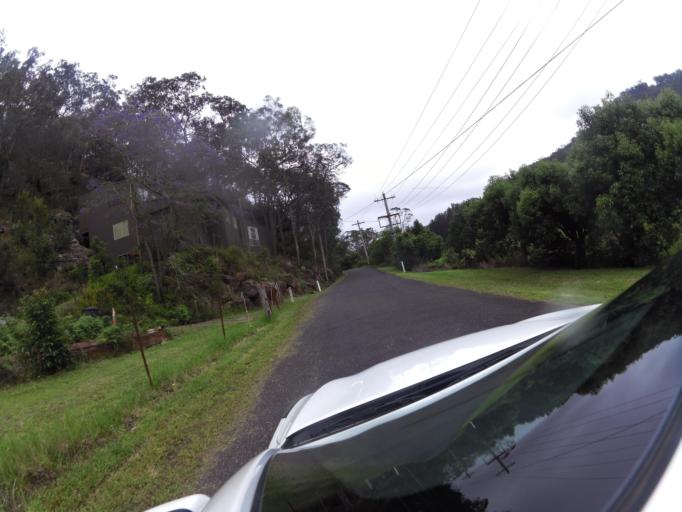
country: AU
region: New South Wales
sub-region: Hornsby Shire
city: Glenorie
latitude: -33.4310
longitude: 150.9594
